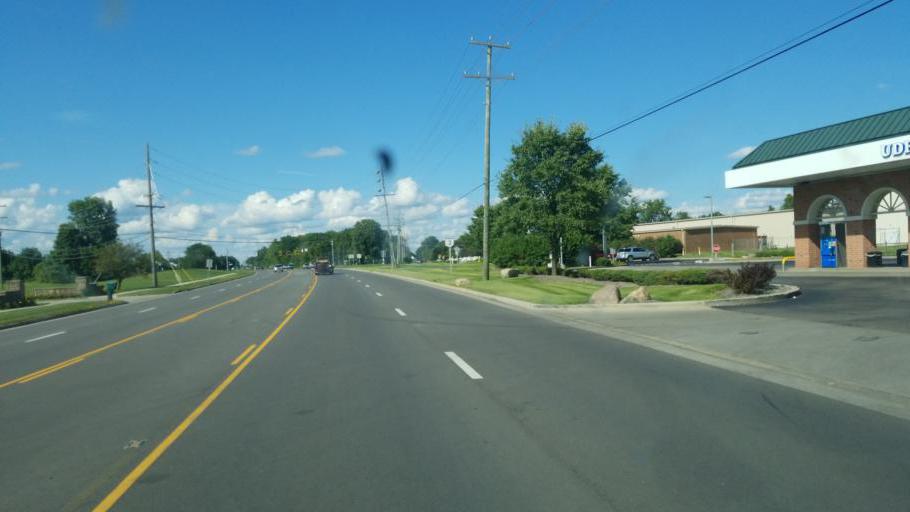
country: US
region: Ohio
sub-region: Franklin County
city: Westerville
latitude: 40.1517
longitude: -82.9208
